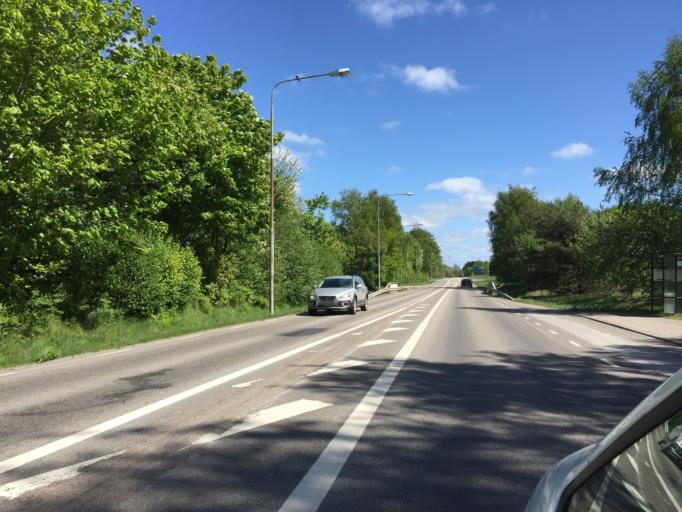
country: SE
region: Halland
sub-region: Varbergs Kommun
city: Varberg
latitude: 57.1113
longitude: 12.2849
